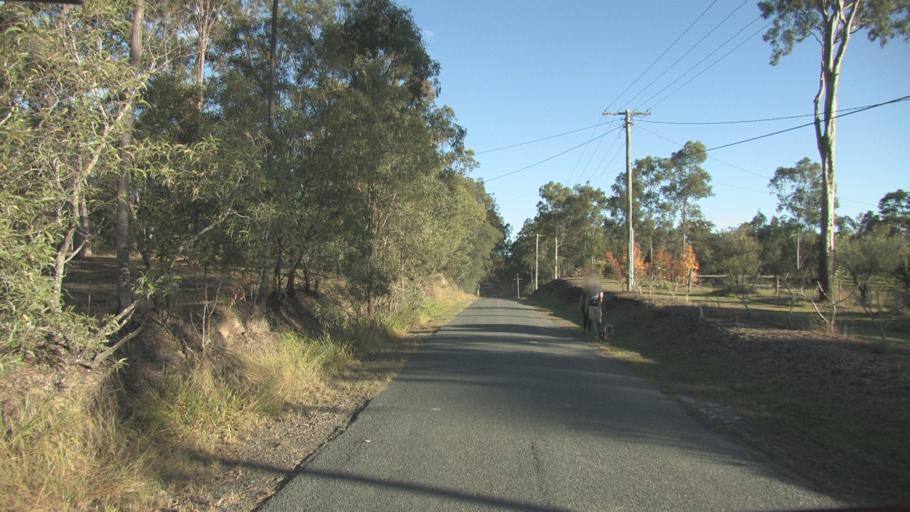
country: AU
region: Queensland
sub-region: Logan
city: Waterford West
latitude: -27.7342
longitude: 153.1514
